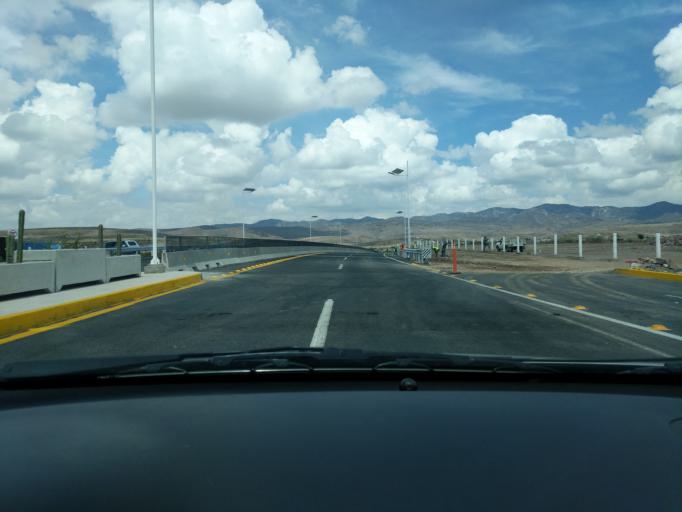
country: MX
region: San Luis Potosi
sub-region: Mexquitic de Carmona
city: Guadalupe Victoria
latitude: 22.1645
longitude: -101.0568
